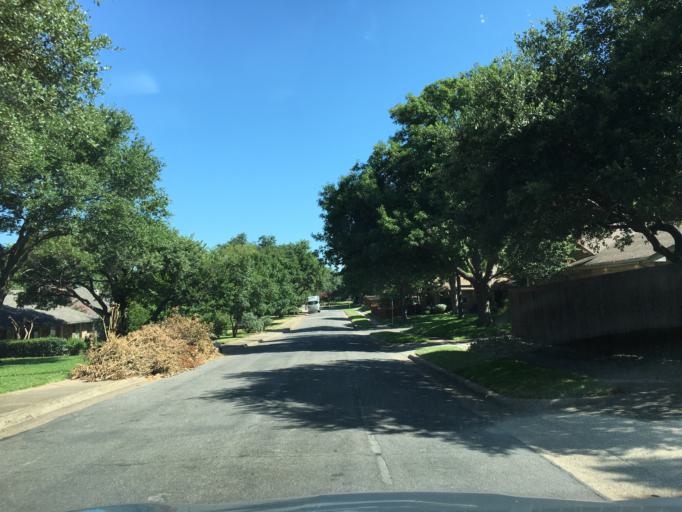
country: US
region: Texas
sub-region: Dallas County
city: Garland
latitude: 32.8672
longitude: -96.6950
